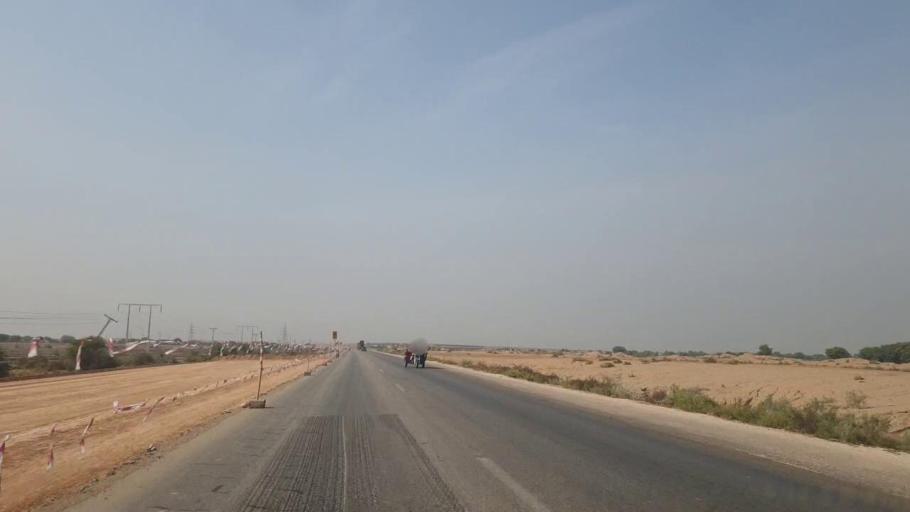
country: PK
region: Sindh
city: Sann
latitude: 26.1479
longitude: 68.0311
